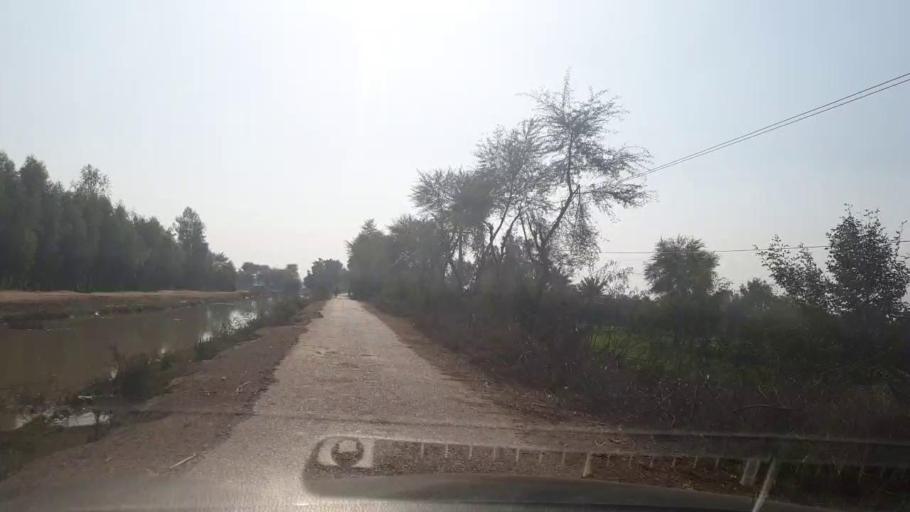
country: PK
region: Sindh
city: Ubauro
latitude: 28.1380
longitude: 69.6491
